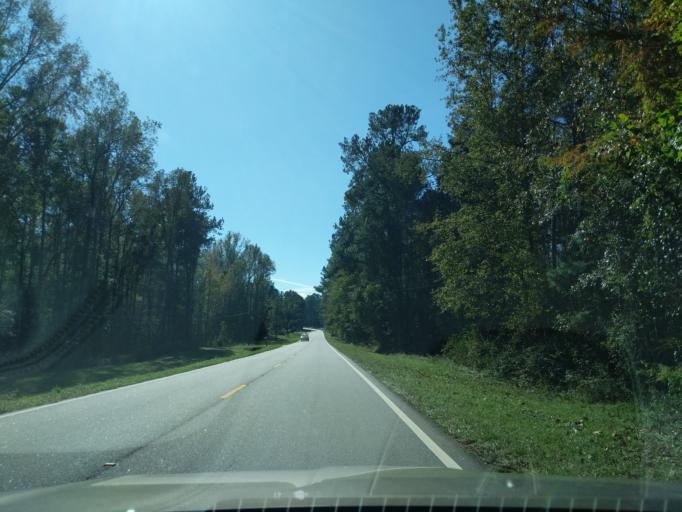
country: US
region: Georgia
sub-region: Richmond County
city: Hephzibah
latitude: 33.2908
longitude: -82.0227
